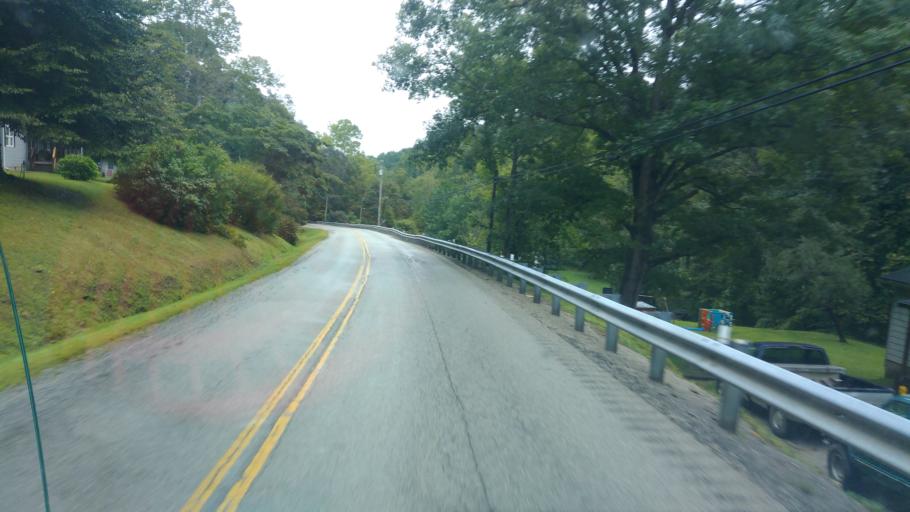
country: US
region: Kentucky
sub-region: Fleming County
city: Flemingsburg
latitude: 38.4504
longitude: -83.5182
